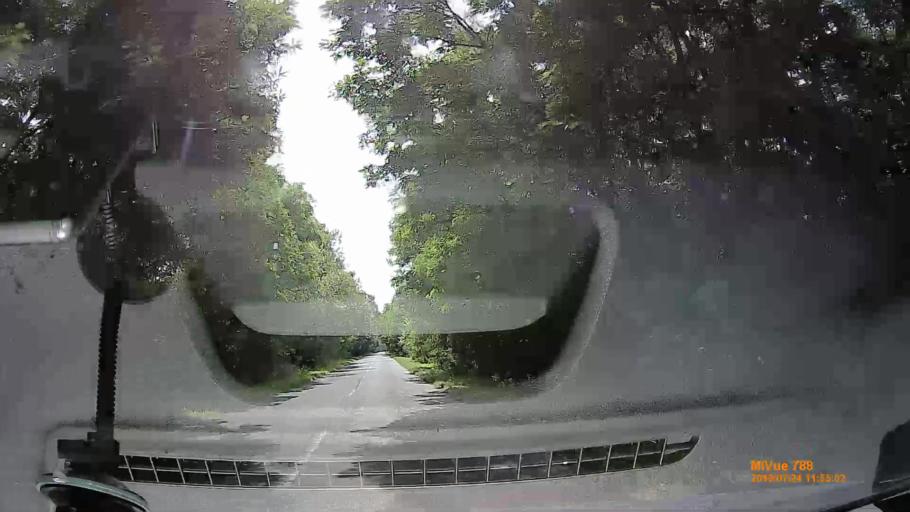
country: HU
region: Szabolcs-Szatmar-Bereg
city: Vasarosnameny
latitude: 48.2134
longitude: 22.4125
